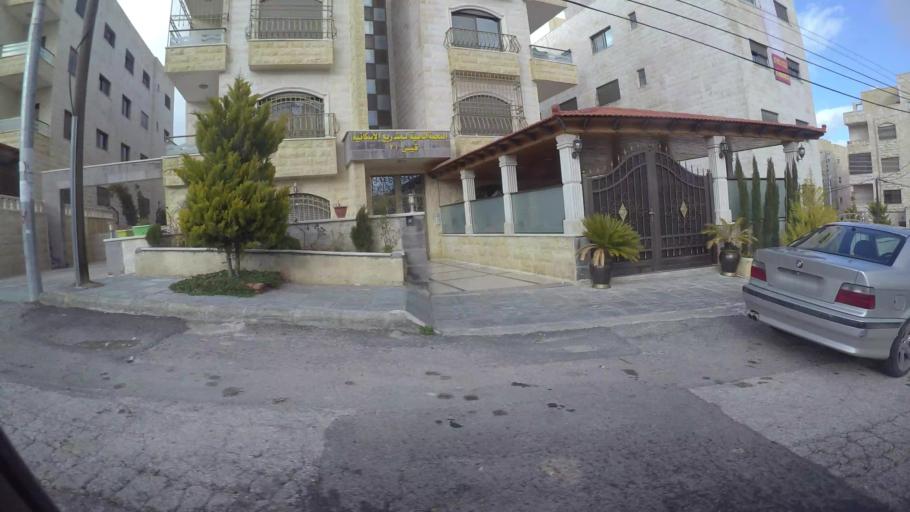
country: JO
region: Amman
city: Al Jubayhah
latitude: 32.0544
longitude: 35.8987
